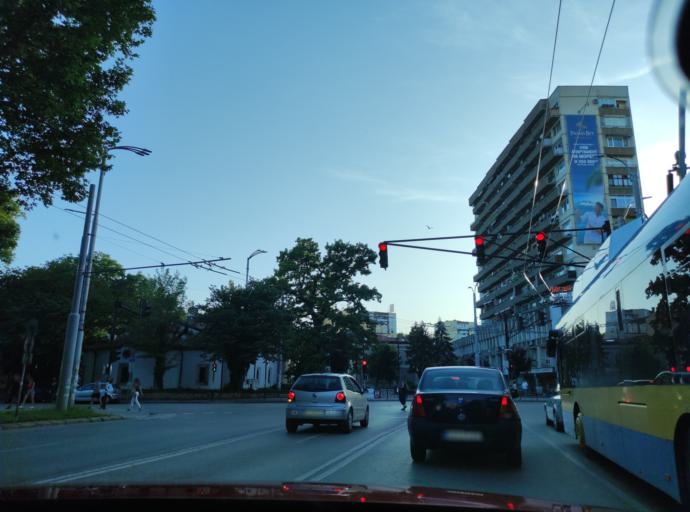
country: BG
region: Pleven
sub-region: Obshtina Pleven
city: Pleven
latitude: 43.4132
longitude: 24.6175
